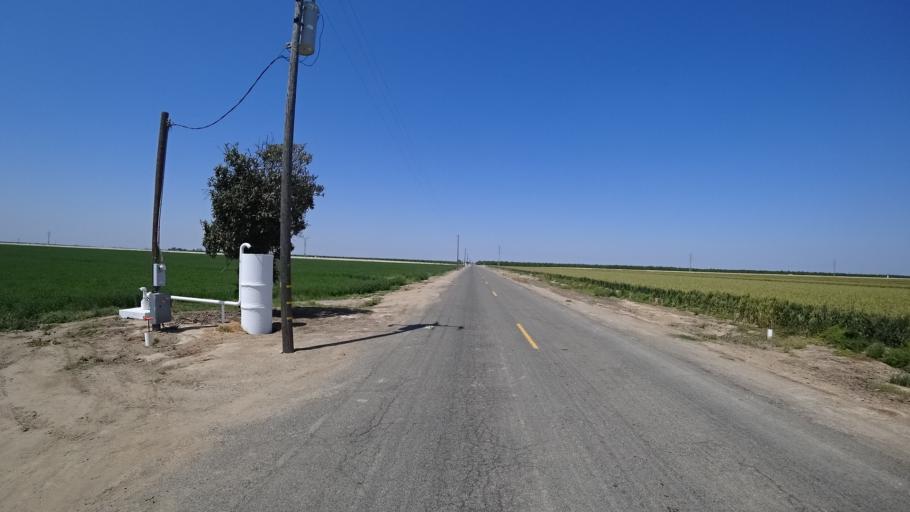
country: US
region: California
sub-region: Kings County
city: Home Garden
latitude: 36.2840
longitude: -119.5876
